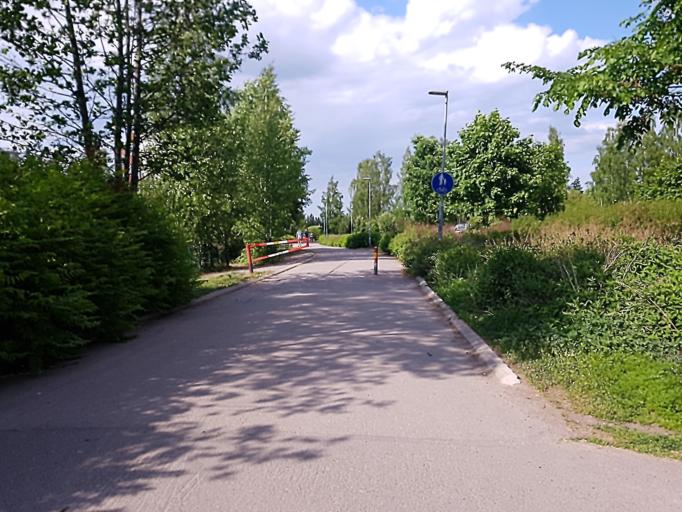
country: FI
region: Uusimaa
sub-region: Helsinki
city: Helsinki
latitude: 60.2323
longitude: 24.9816
